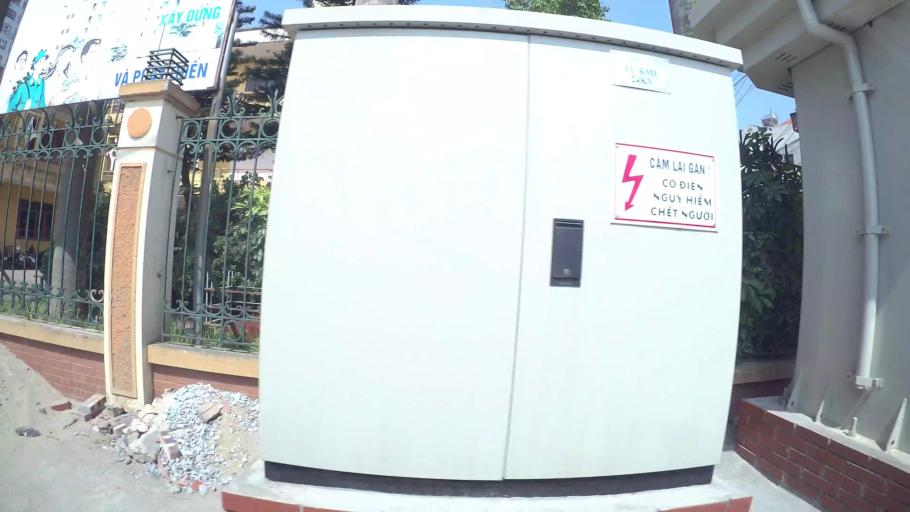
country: VN
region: Ha Noi
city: Hoan Kiem
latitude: 21.0637
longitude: 105.8793
